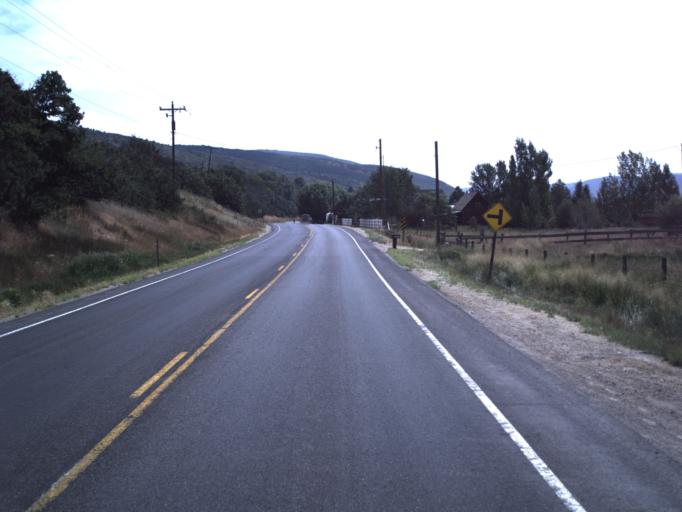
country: US
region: Utah
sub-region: Summit County
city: Francis
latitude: 40.5825
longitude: -111.2327
